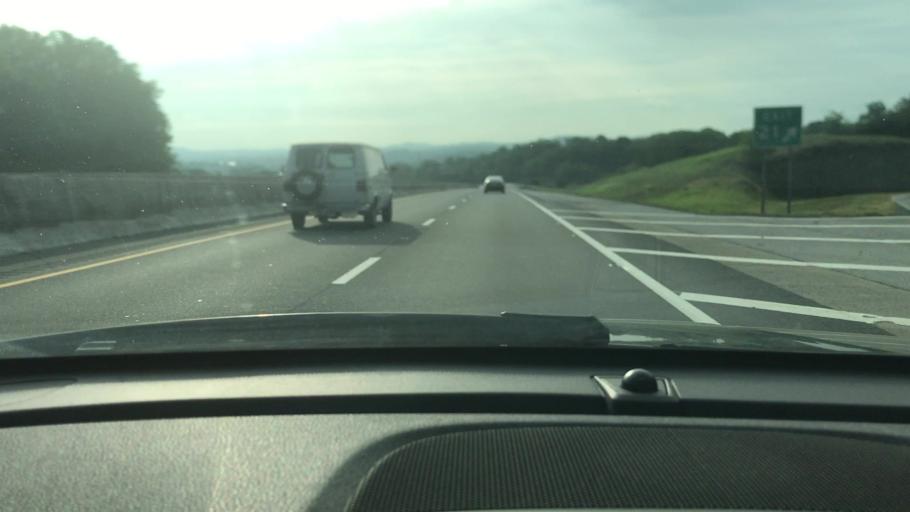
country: US
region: Tennessee
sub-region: Davidson County
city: Nashville
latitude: 36.2295
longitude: -86.8390
